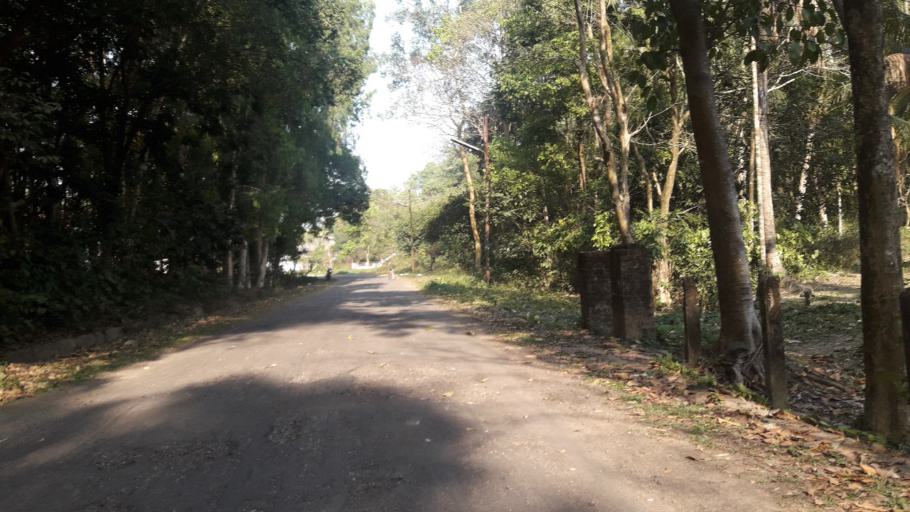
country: BD
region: Chittagong
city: Chittagong
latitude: 22.4666
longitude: 91.7920
